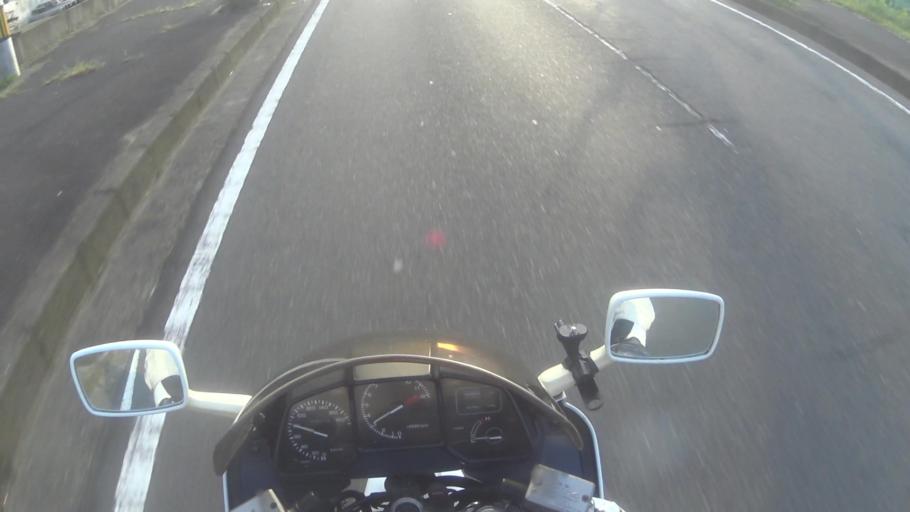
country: JP
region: Kyoto
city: Miyazu
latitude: 35.6031
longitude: 135.0499
